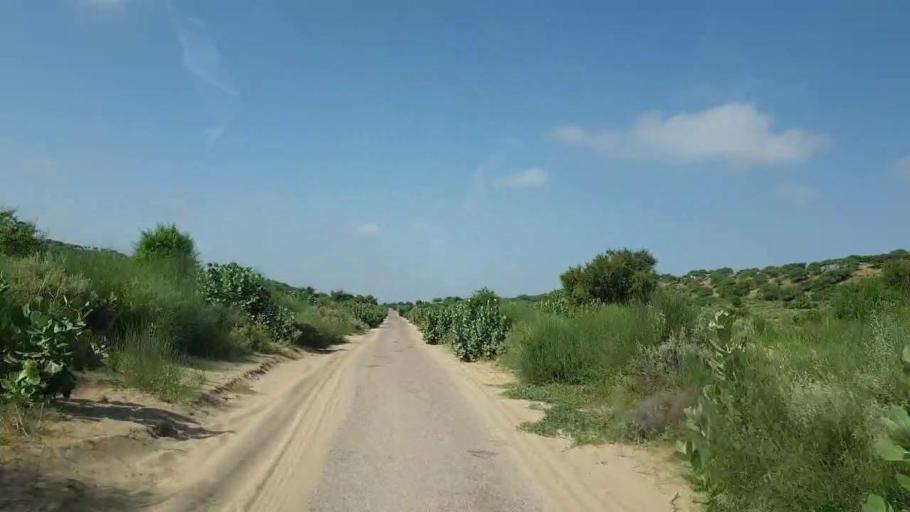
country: PK
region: Sindh
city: Mithi
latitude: 24.5506
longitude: 69.8864
